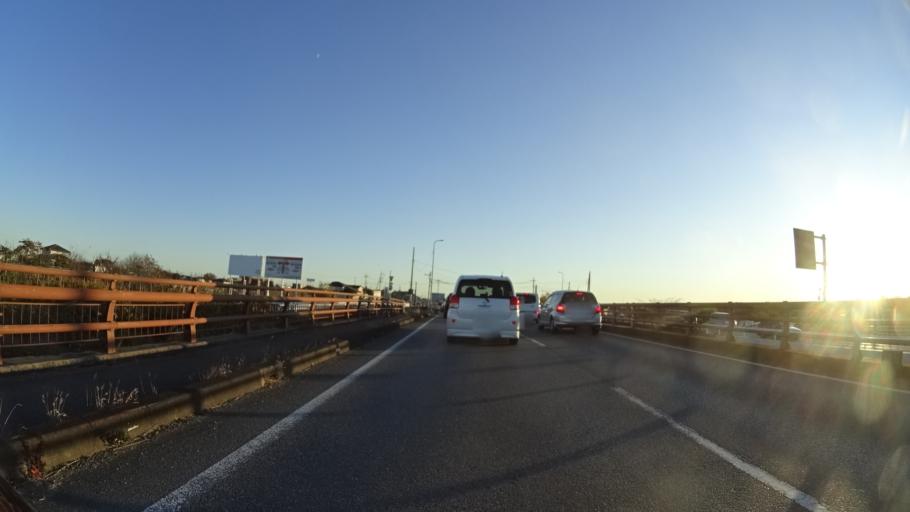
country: JP
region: Tochigi
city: Utsunomiya-shi
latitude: 36.5207
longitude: 139.8409
